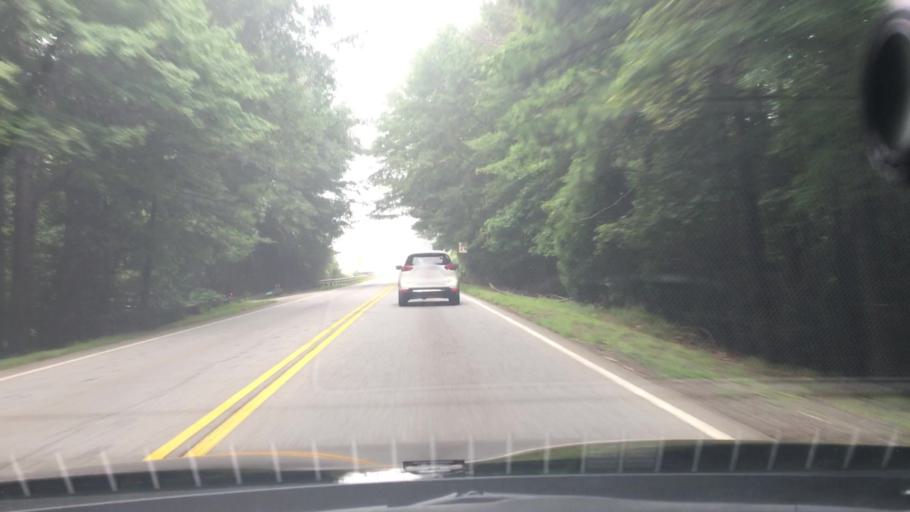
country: US
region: Georgia
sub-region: Coweta County
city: Senoia
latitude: 33.2968
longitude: -84.5416
